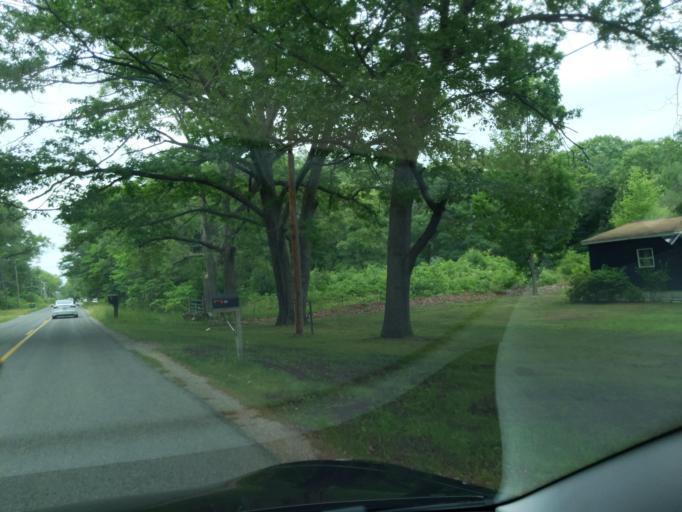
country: US
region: Michigan
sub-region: Muskegon County
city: North Muskegon
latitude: 43.2526
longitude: -86.3222
